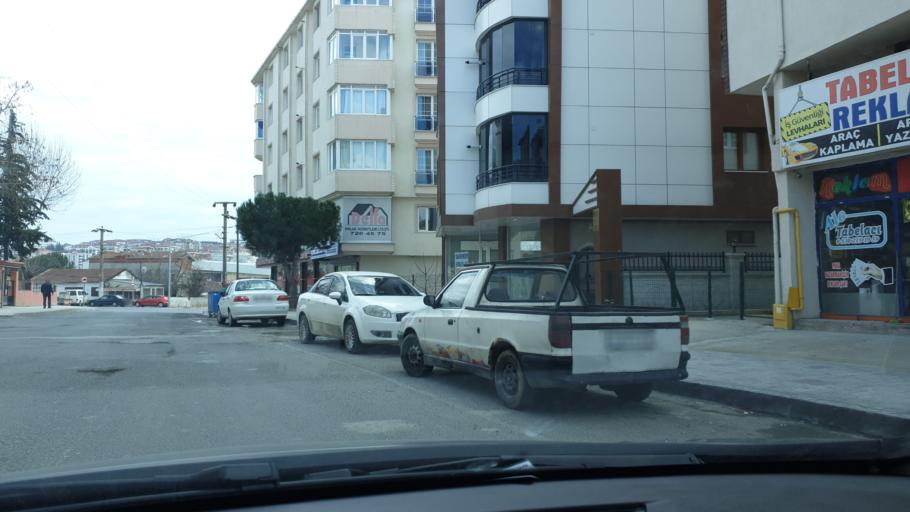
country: TR
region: Tekirdag
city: Cerkezkoey
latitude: 41.2823
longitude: 27.9961
